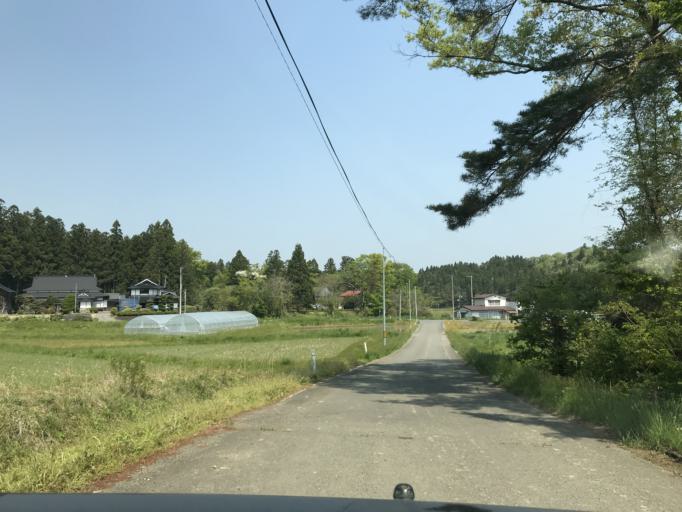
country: JP
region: Iwate
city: Ichinoseki
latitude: 38.8586
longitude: 141.0646
